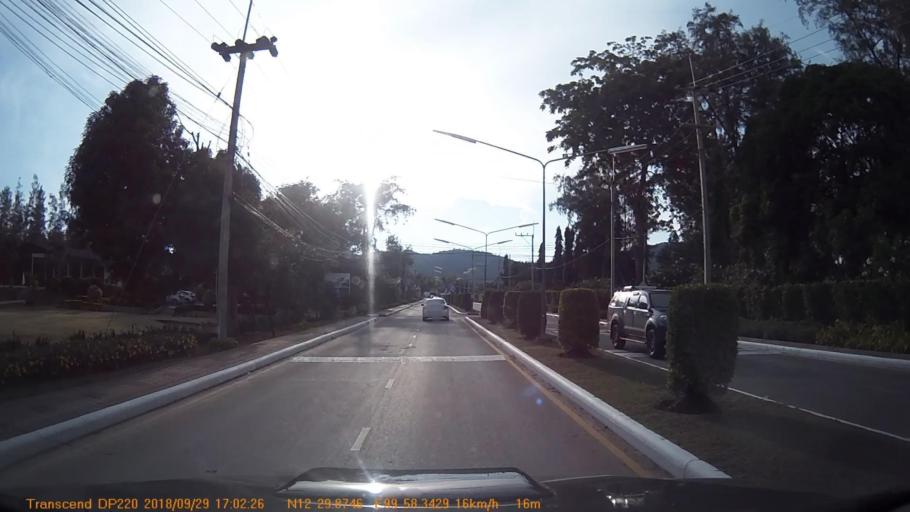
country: TH
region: Prachuap Khiri Khan
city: Hua Hin
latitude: 12.4979
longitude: 99.9722
